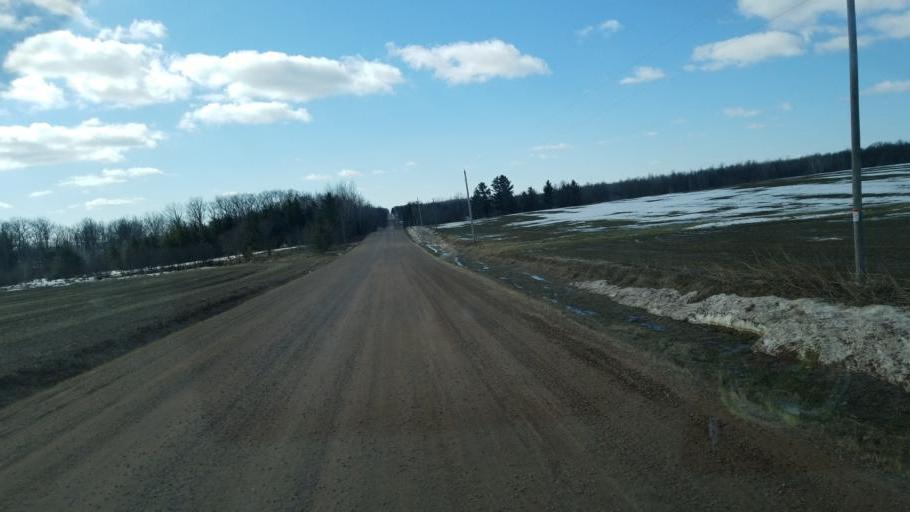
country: US
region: Wisconsin
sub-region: Clark County
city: Loyal
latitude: 44.6828
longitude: -90.4558
